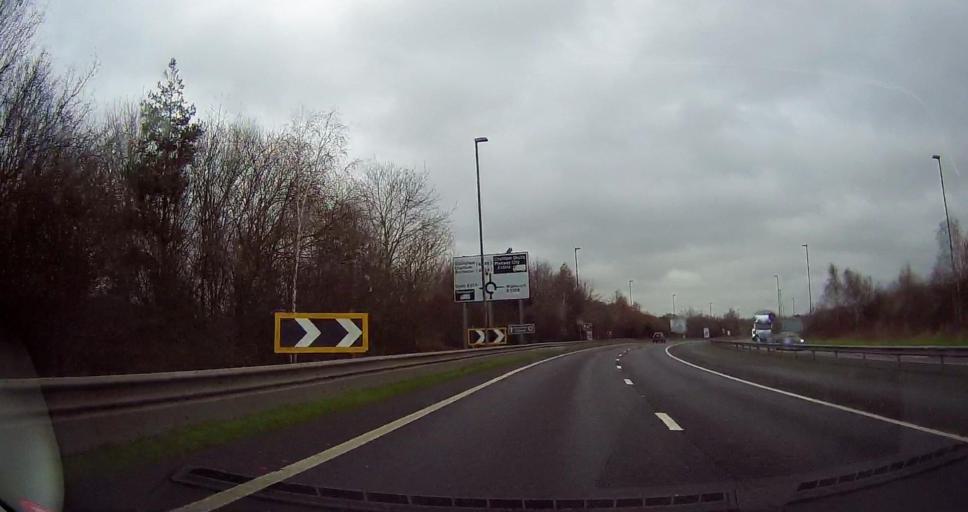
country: GB
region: England
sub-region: Kent
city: Strood
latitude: 51.4157
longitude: 0.5124
